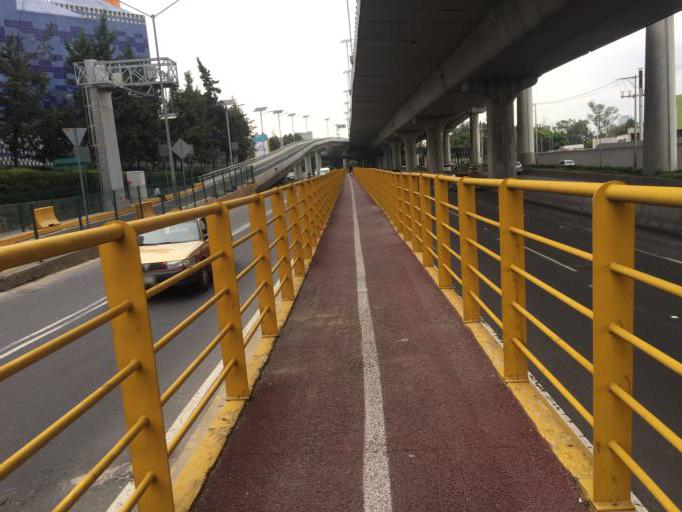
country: MX
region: Mexico City
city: Polanco
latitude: 19.4109
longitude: -99.1940
